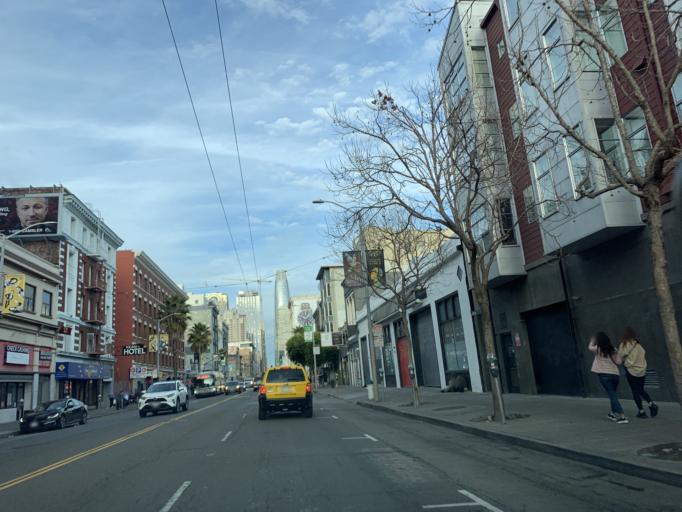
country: US
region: California
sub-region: San Francisco County
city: San Francisco
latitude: 37.7802
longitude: -122.4096
